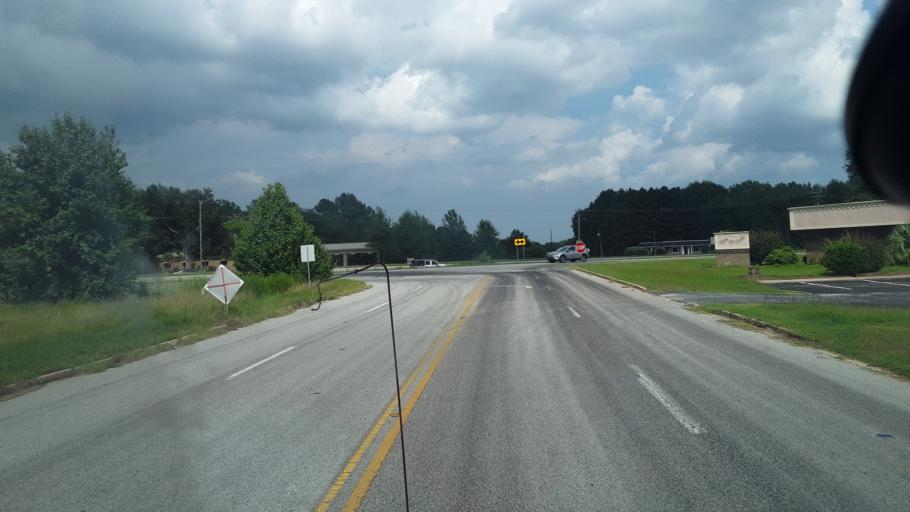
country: US
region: South Carolina
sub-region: Sumter County
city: Sumter
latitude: 33.9564
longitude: -80.3747
